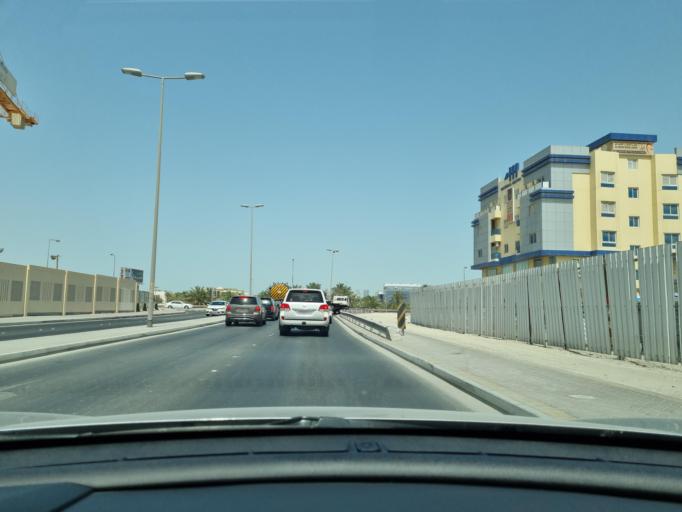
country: BH
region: Manama
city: Jidd Hafs
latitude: 26.1961
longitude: 50.5561
